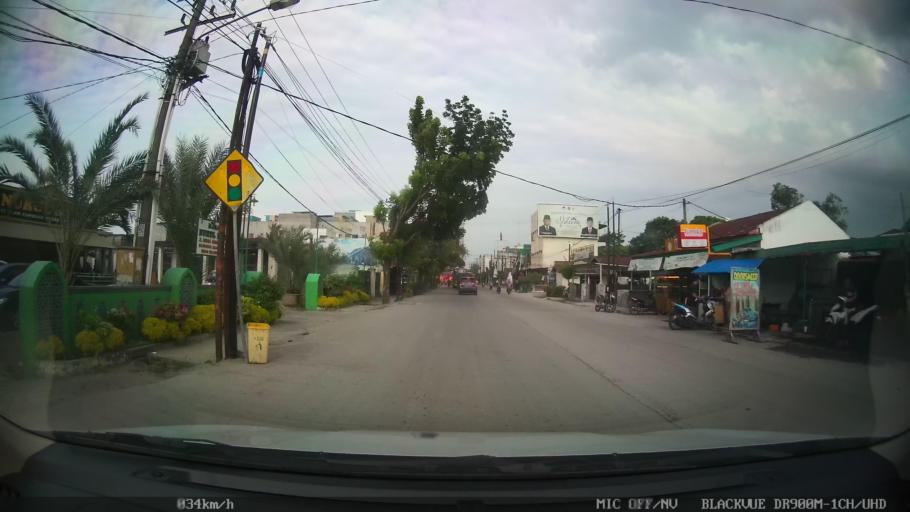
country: ID
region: North Sumatra
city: Sunggal
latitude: 3.5629
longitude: 98.6249
